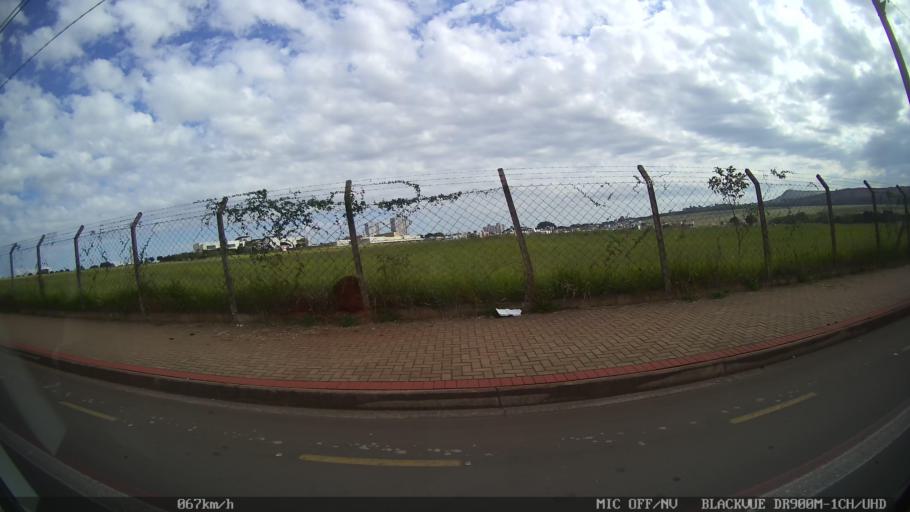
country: BR
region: Sao Paulo
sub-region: Limeira
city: Limeira
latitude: -22.5513
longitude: -47.4271
